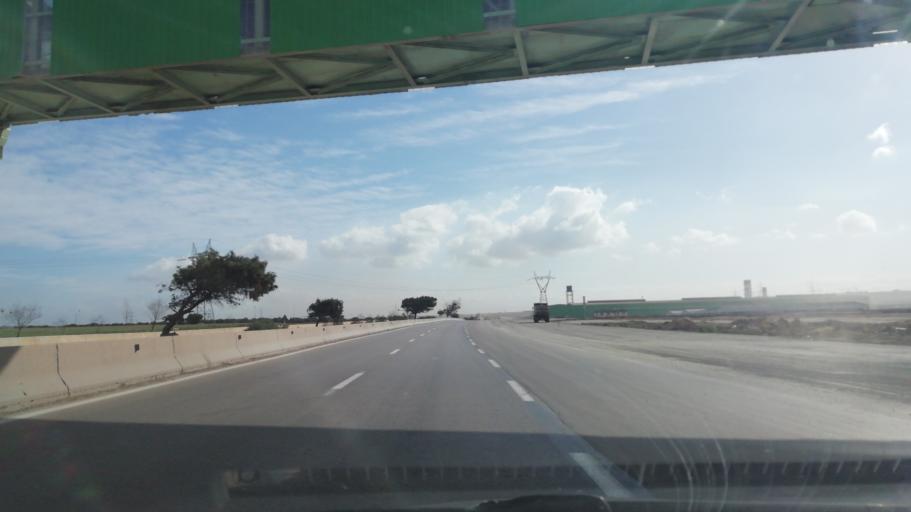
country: DZ
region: Oran
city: Ain el Bya
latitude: 35.7785
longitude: -0.2652
